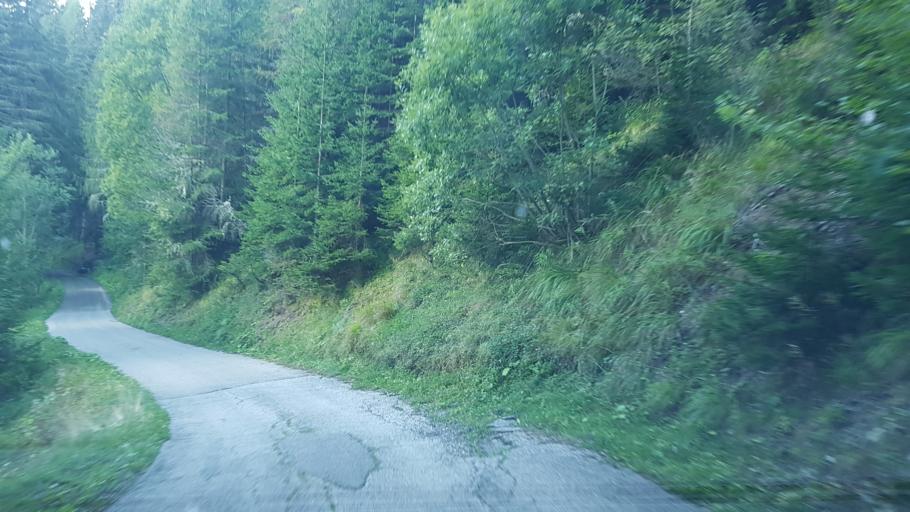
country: IT
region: Veneto
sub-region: Provincia di Belluno
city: San Pietro di Cadore
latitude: 46.5871
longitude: 12.5926
